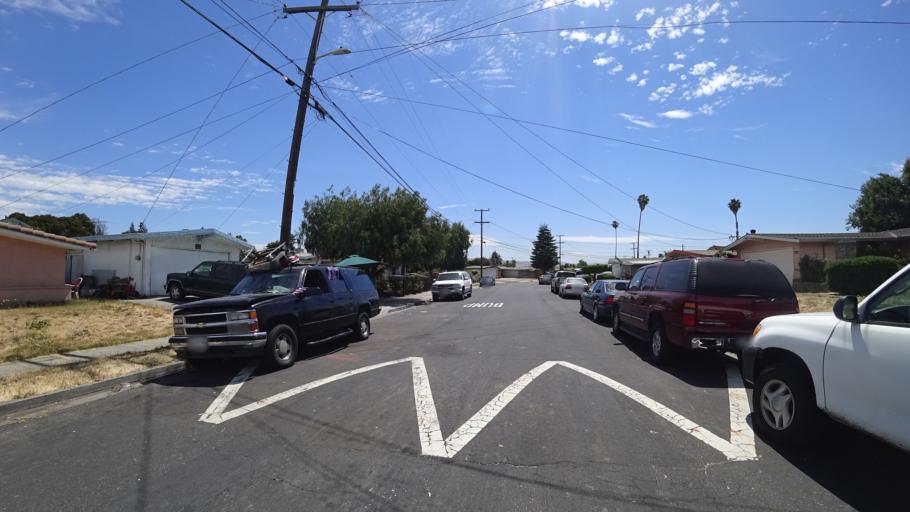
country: US
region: California
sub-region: Alameda County
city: Hayward
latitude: 37.6304
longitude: -122.0880
